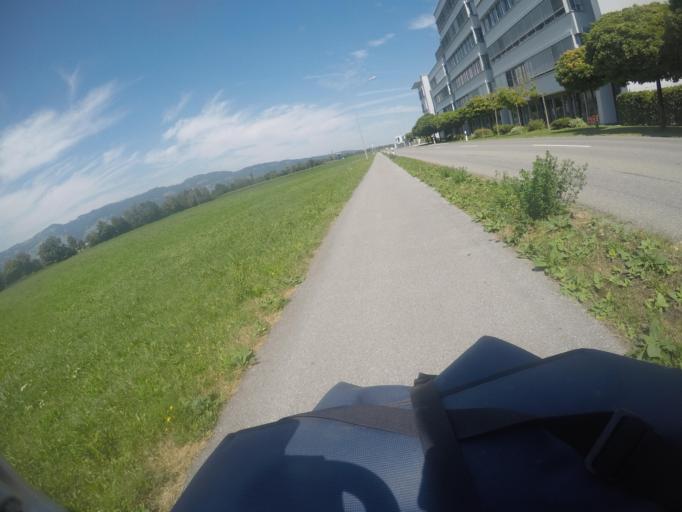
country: AT
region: Vorarlberg
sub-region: Politischer Bezirk Feldkirch
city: Koblach
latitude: 47.3471
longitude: 9.5887
